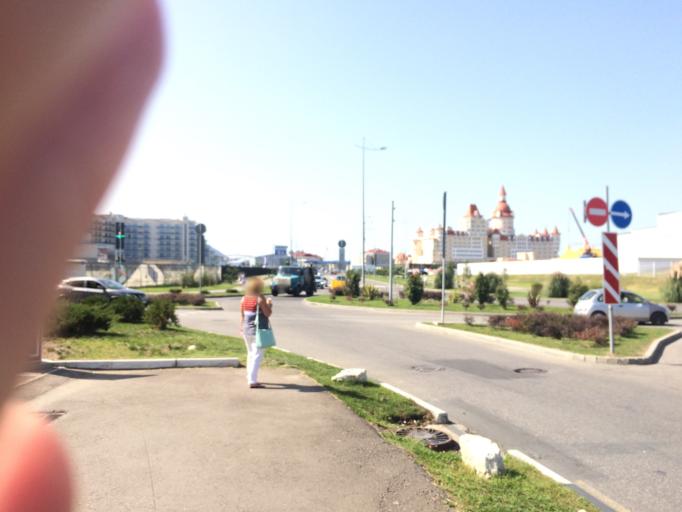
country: RU
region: Krasnodarskiy
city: Adler
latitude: 43.4007
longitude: 39.9684
